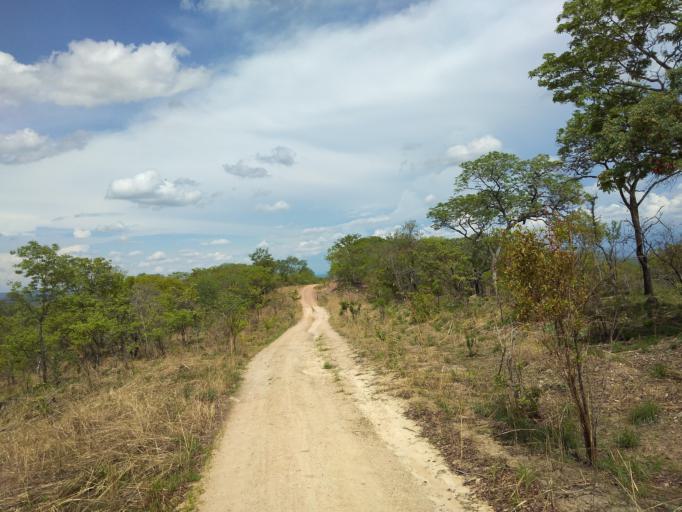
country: ZM
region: Eastern
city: Nyimba
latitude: -14.1170
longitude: 30.1044
